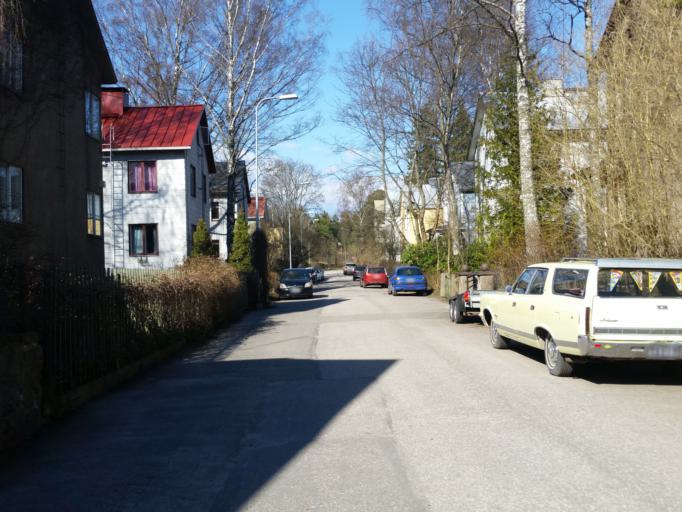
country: FI
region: Uusimaa
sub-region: Helsinki
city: Helsinki
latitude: 60.2215
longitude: 24.9685
